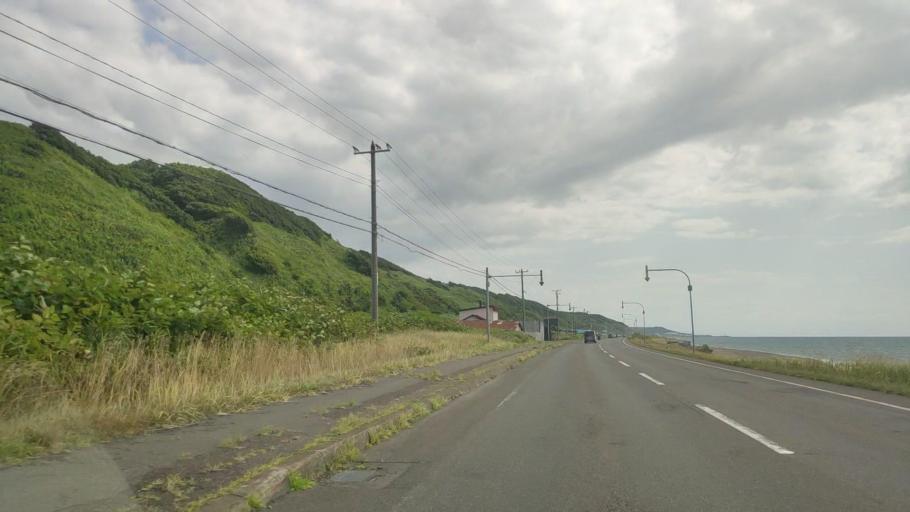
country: JP
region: Hokkaido
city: Rumoi
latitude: 44.1926
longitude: 141.6584
